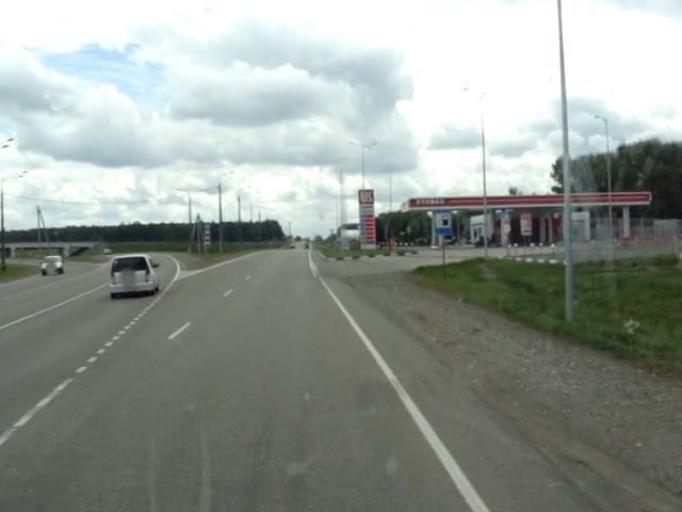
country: RU
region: Altai Krai
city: Zarya
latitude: 52.5803
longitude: 85.1759
